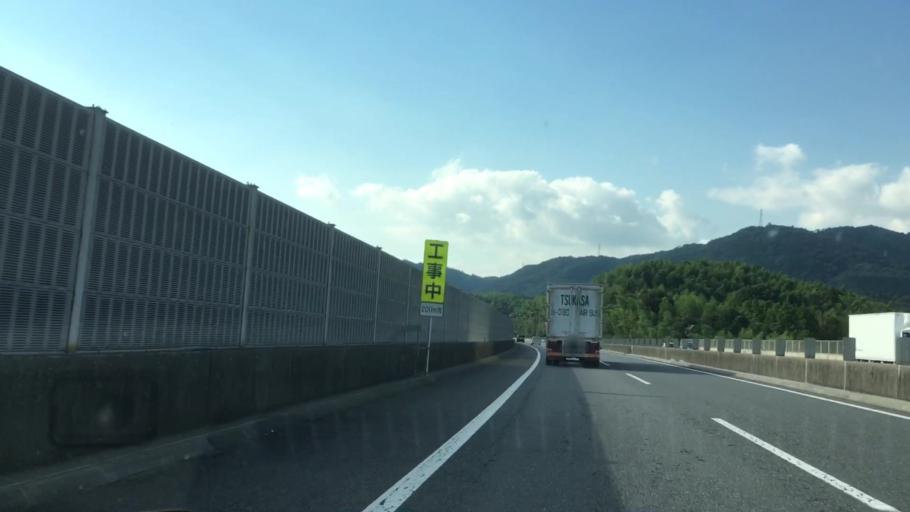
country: JP
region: Yamaguchi
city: Kudamatsu
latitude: 34.0389
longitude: 131.9230
